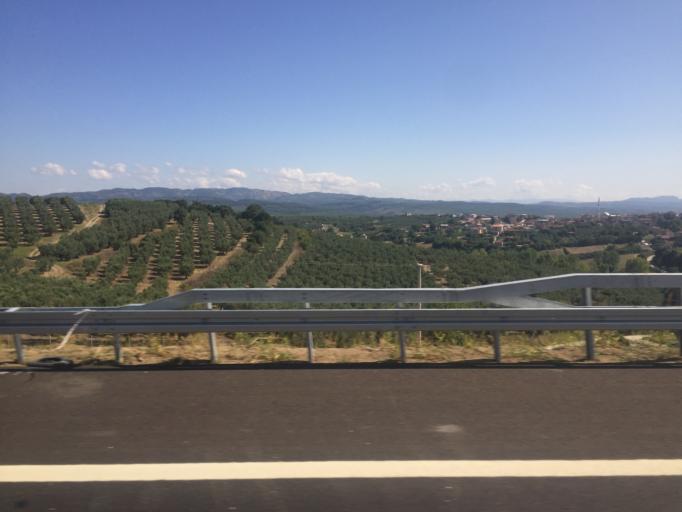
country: TR
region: Bursa
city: Gorukle
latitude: 40.2512
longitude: 28.7478
